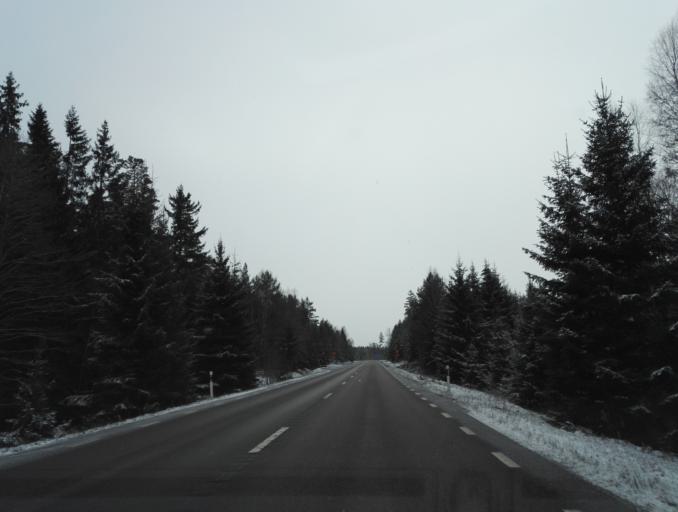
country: SE
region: Kronoberg
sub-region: Uppvidinge Kommun
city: Aseda
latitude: 57.1680
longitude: 15.4926
